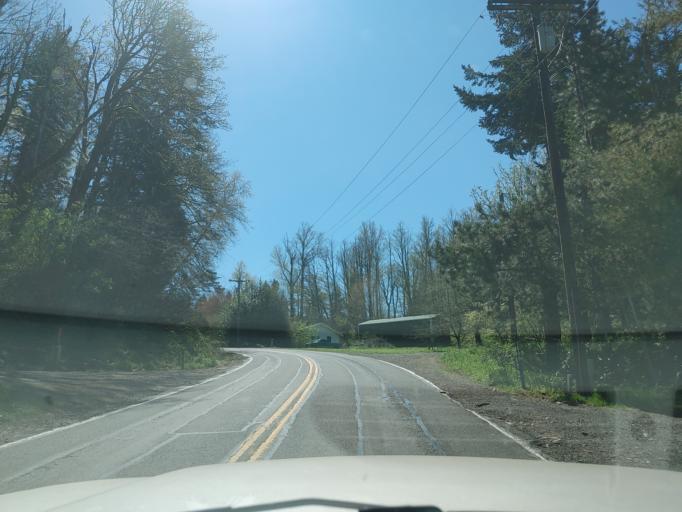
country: US
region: Washington
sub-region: Clark County
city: Washougal
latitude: 45.5344
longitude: -122.2905
